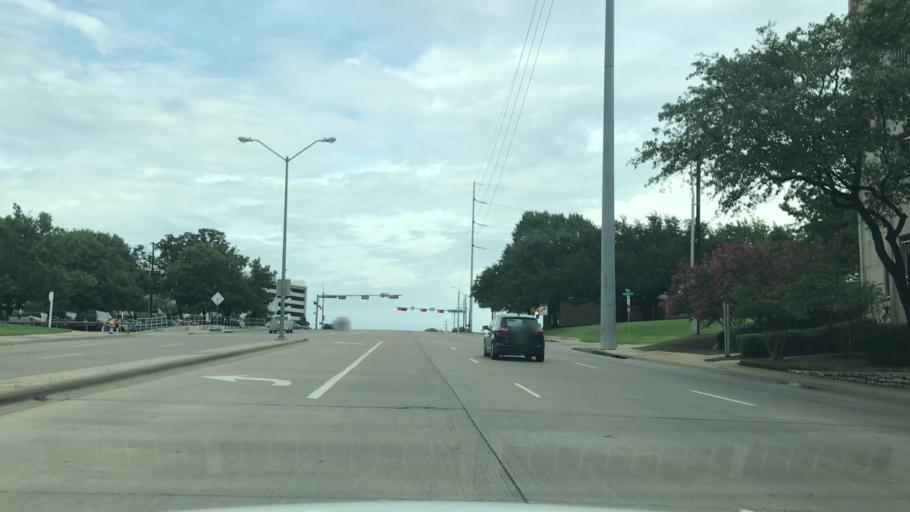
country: US
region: Texas
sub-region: Dallas County
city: Dallas
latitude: 32.8089
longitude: -96.8362
